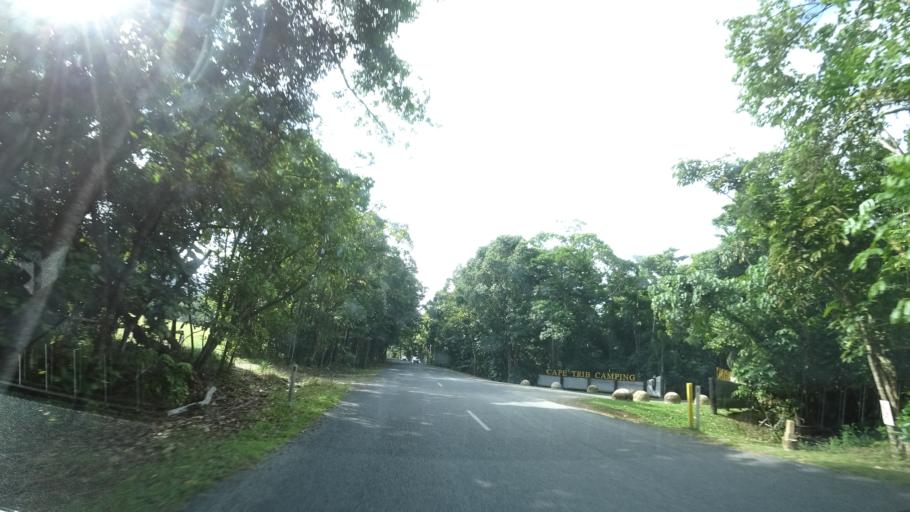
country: AU
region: Queensland
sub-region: Cairns
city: Port Douglas
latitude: -16.0956
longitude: 145.4598
